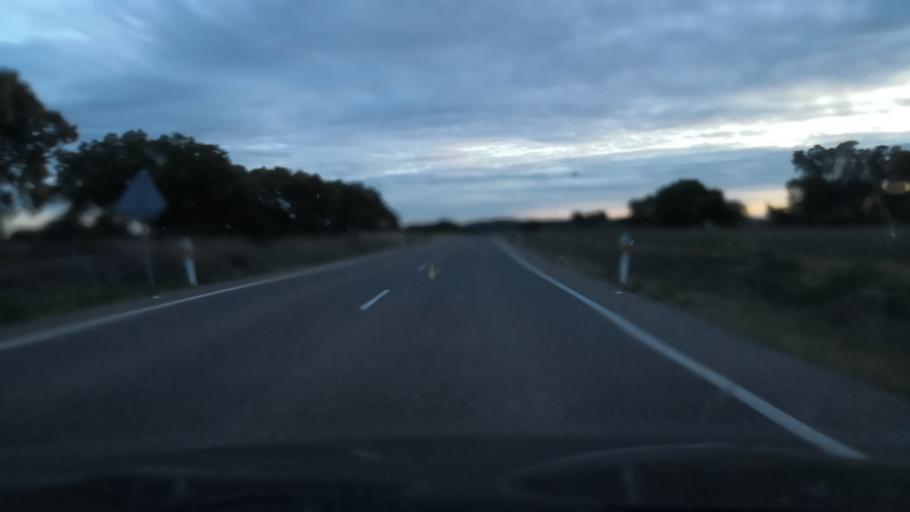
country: ES
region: Extremadura
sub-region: Provincia de Badajoz
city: La Roca de la Sierra
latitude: 39.0659
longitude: -6.7618
